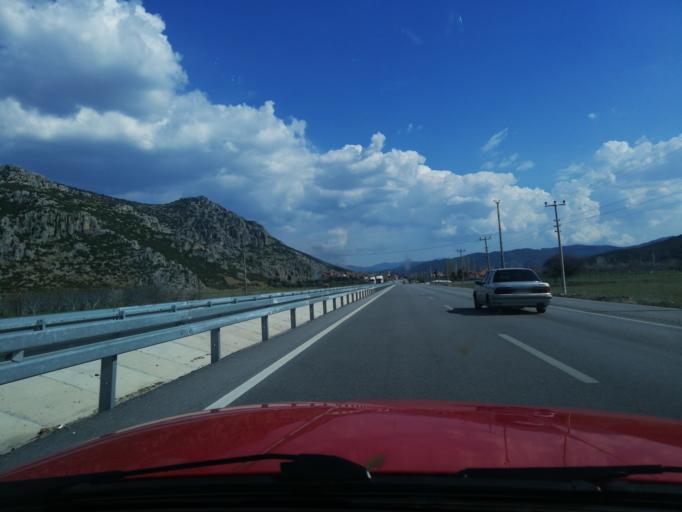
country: TR
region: Burdur
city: Celtikci
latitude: 37.5444
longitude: 30.4694
